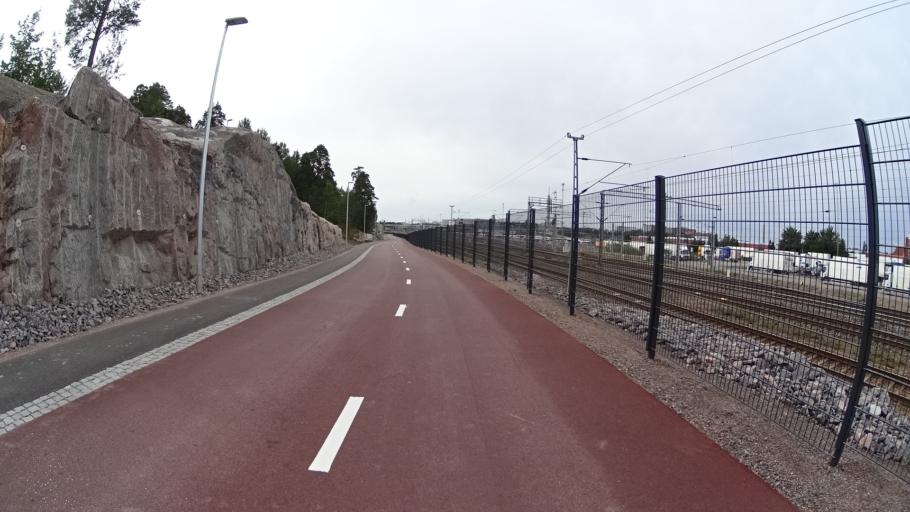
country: FI
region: Uusimaa
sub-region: Helsinki
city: Helsinki
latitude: 60.2138
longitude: 24.9373
